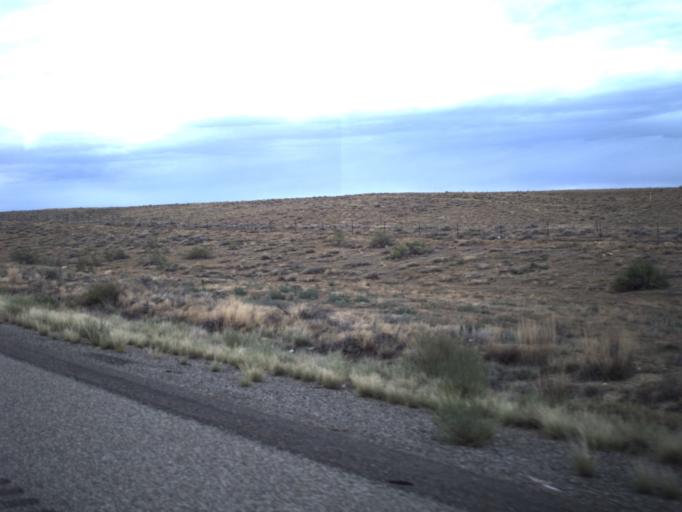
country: US
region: Colorado
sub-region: Mesa County
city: Loma
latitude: 39.1390
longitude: -109.1556
